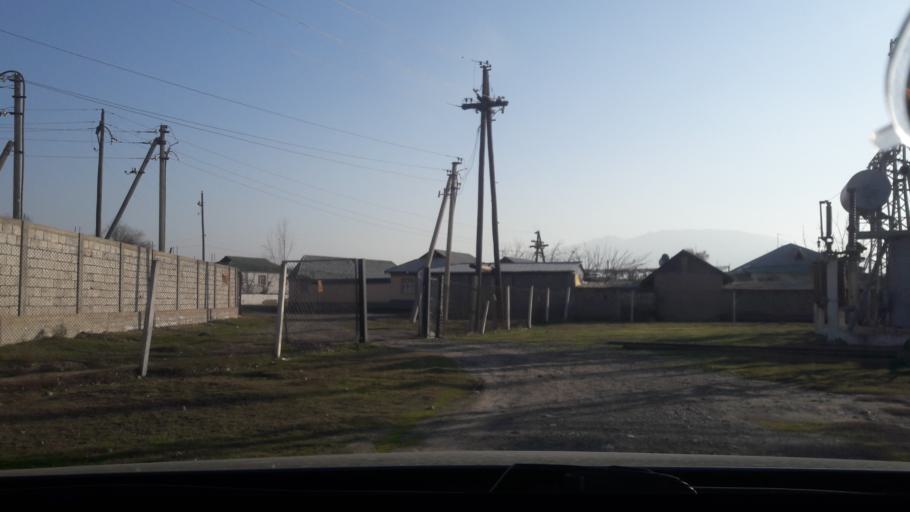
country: TJ
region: Khatlon
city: Vose'
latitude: 37.8160
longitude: 69.6441
